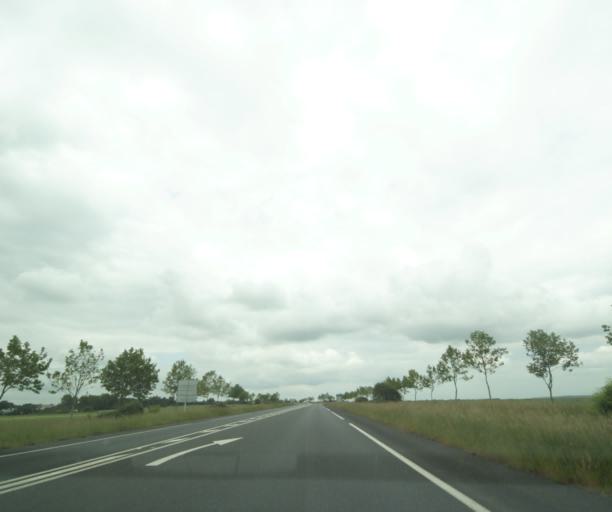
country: FR
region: Poitou-Charentes
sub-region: Departement des Deux-Sevres
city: Saint-Varent
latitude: 46.8989
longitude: -0.1918
